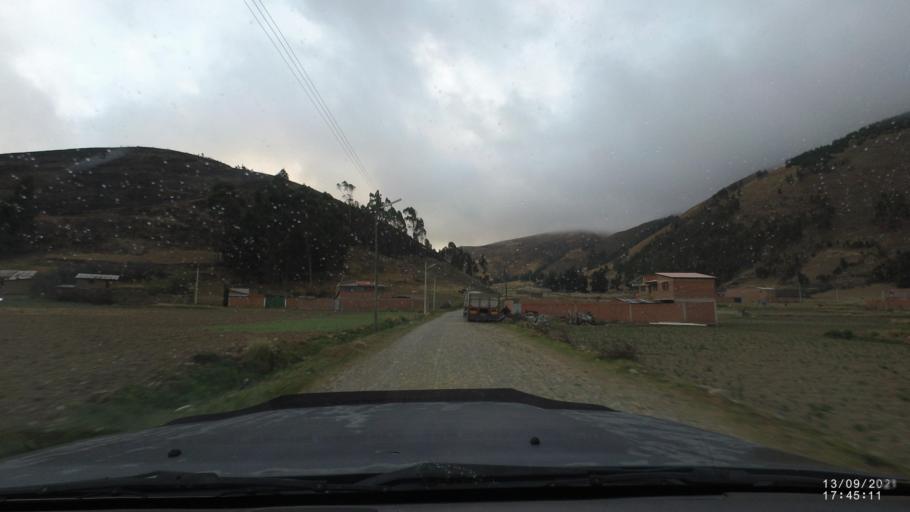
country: BO
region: Cochabamba
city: Colomi
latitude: -17.3762
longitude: -65.8317
